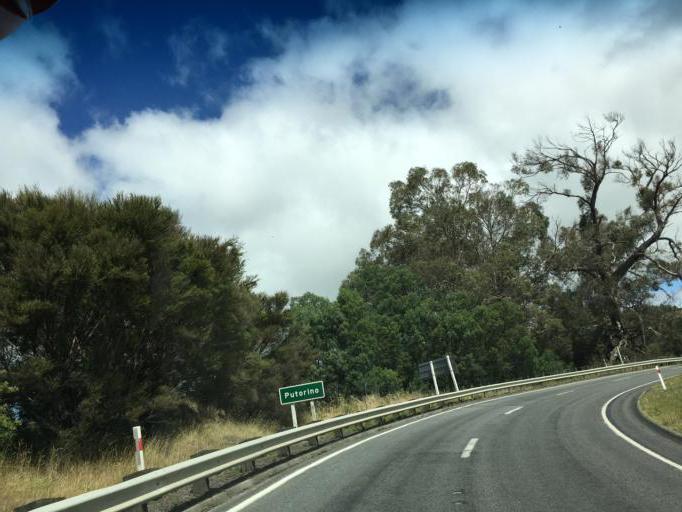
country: NZ
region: Hawke's Bay
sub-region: Napier City
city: Napier
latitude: -39.1313
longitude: 177.0052
